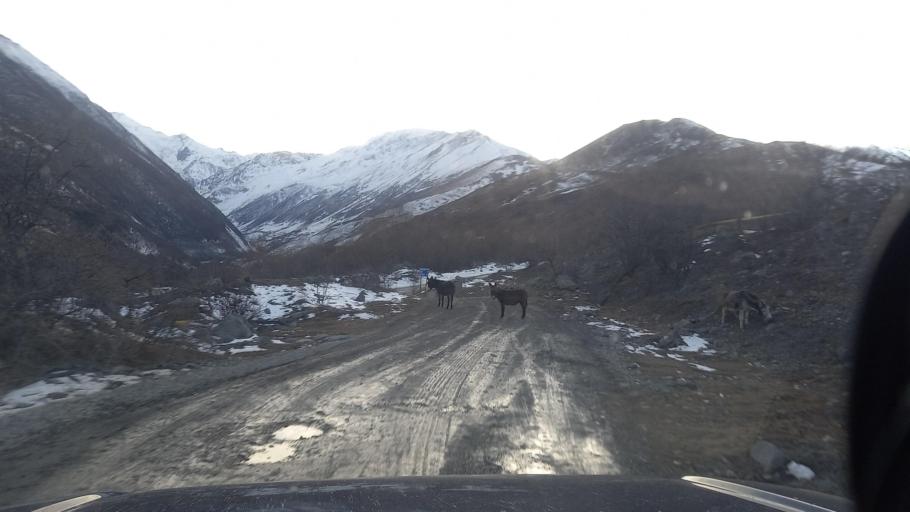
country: RU
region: Ingushetiya
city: Dzhayrakh
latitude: 42.8394
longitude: 44.5114
